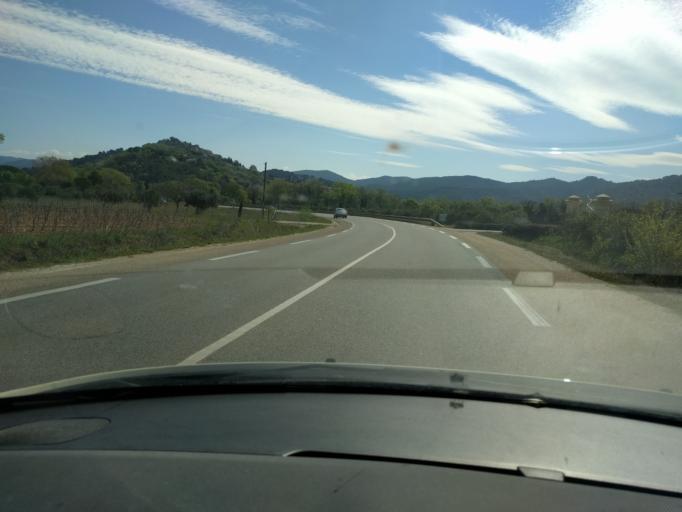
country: FR
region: Provence-Alpes-Cote d'Azur
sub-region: Departement du Var
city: Pierrefeu-du-Var
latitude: 43.2257
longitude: 6.1286
